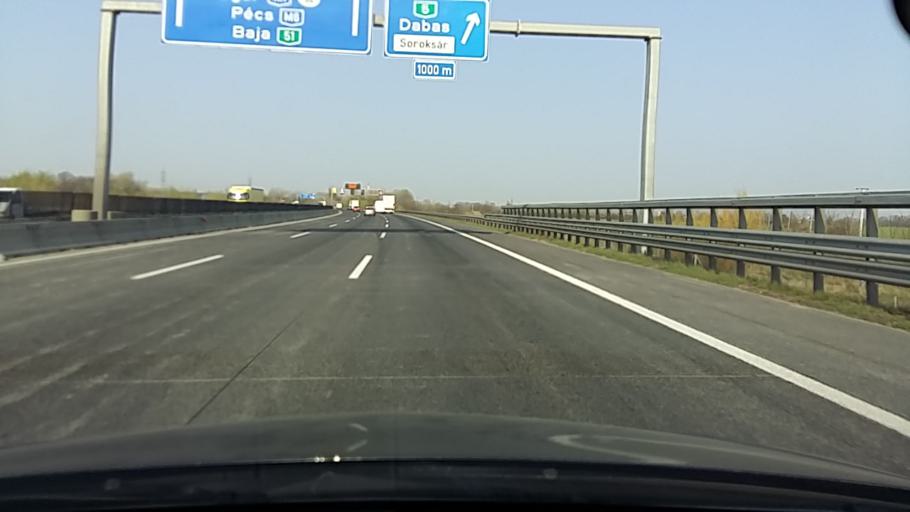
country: HU
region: Pest
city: Alsonemedi
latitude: 47.3670
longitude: 19.1656
